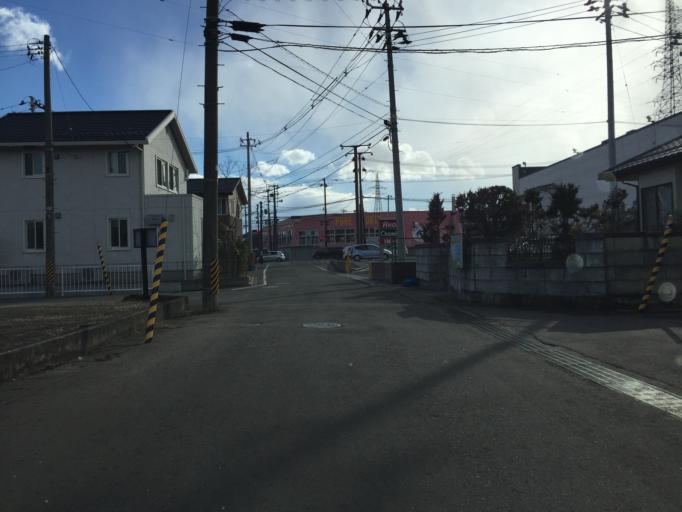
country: JP
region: Fukushima
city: Fukushima-shi
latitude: 37.7301
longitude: 140.4458
